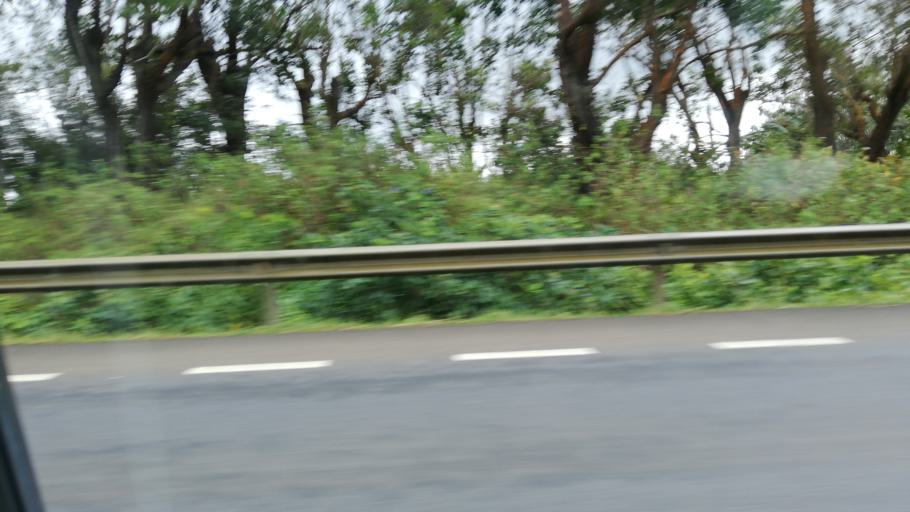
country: MU
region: Plaines Wilhems
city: Curepipe
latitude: -20.2936
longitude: 57.5436
